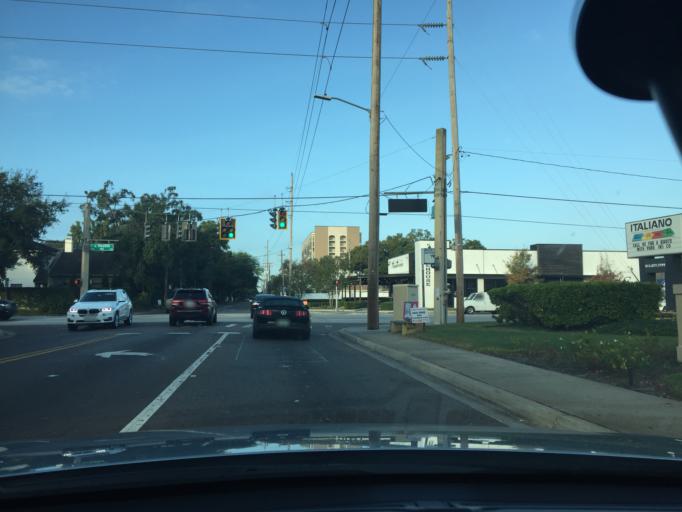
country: US
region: Florida
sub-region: Hillsborough County
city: Tampa
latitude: 27.9375
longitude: -82.4929
